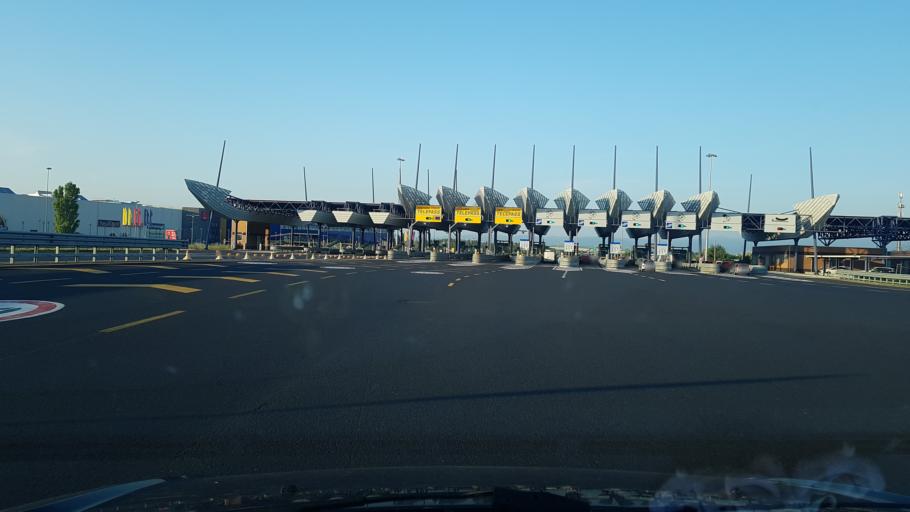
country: IT
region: Friuli Venezia Giulia
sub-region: Provincia di Gorizia
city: Villesse
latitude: 45.8622
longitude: 13.4310
